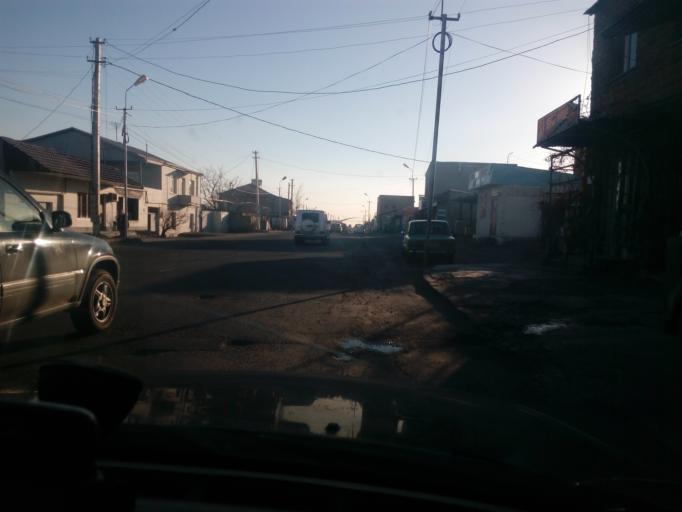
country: AM
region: Kotayk'i Marz
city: Balahovit
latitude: 40.2639
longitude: 44.6101
